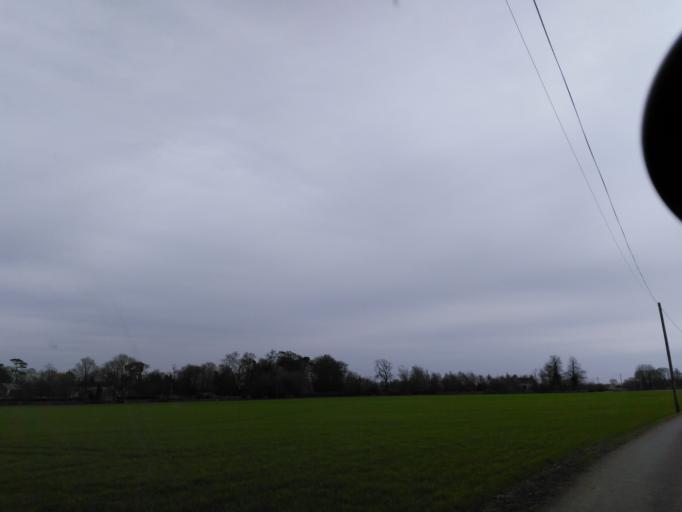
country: GB
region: England
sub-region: Wiltshire
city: Biddestone
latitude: 51.4374
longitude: -2.2111
